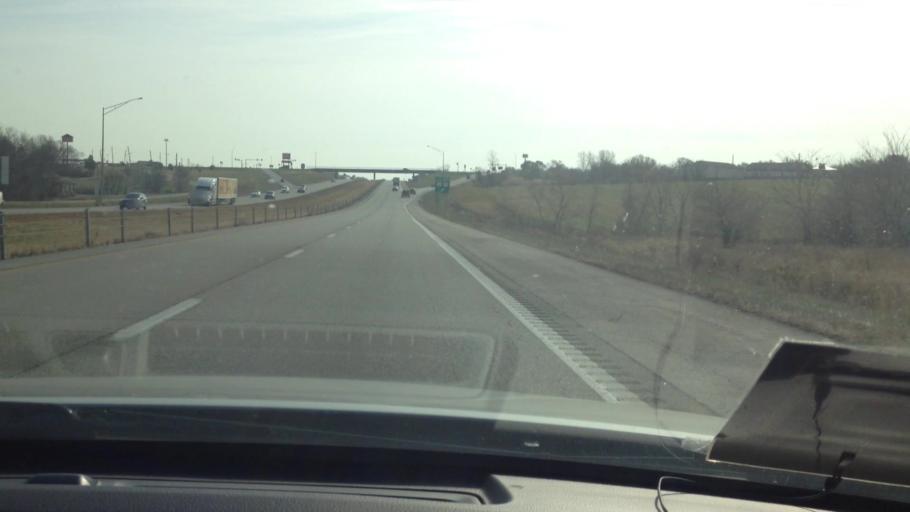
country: US
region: Missouri
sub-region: Cass County
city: Peculiar
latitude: 38.7278
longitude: -94.4597
